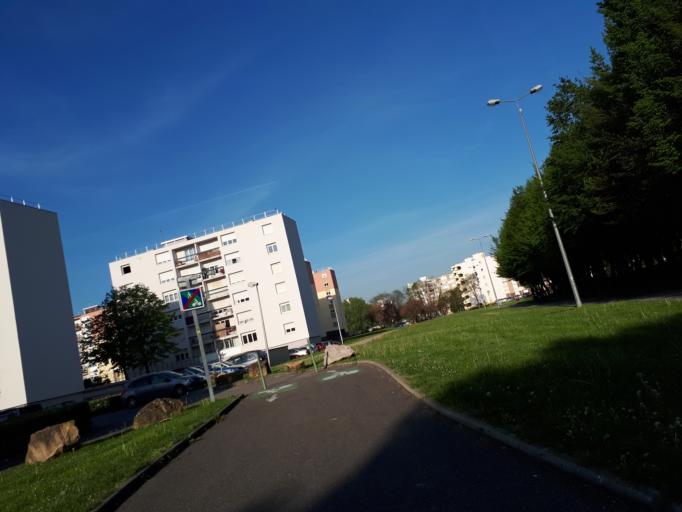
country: FR
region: Rhone-Alpes
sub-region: Departement de l'Isere
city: Bourgoin-Jallieu
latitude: 45.6089
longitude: 5.2687
